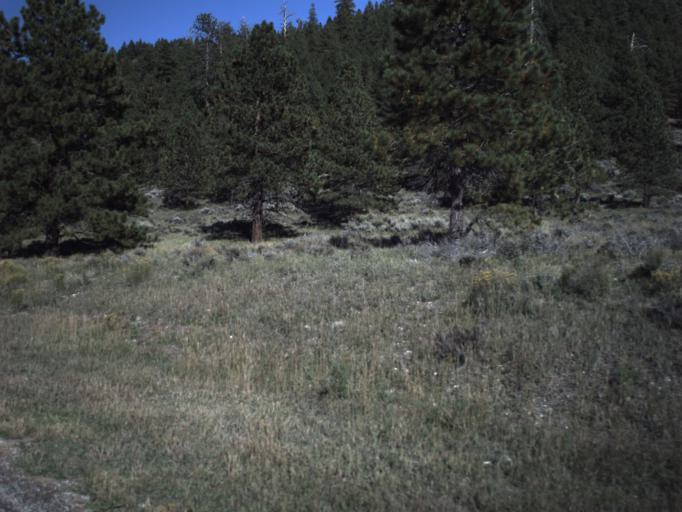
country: US
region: Utah
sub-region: Garfield County
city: Panguitch
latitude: 37.7100
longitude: -112.6248
